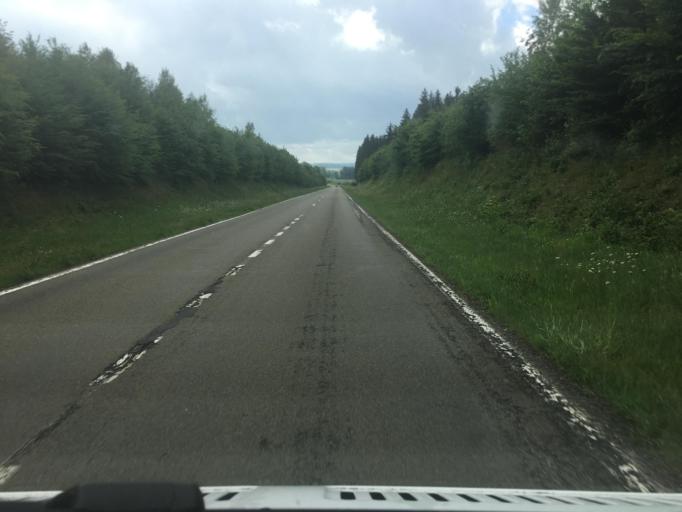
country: BE
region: Wallonia
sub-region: Province du Luxembourg
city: Florenville
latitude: 49.6630
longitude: 5.3312
